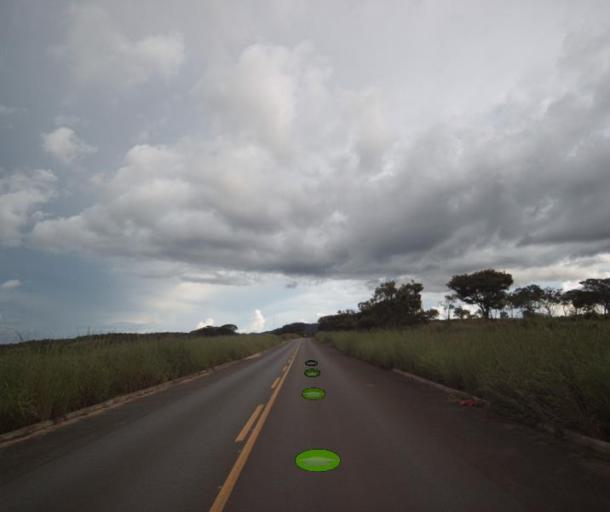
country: BR
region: Goias
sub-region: Niquelandia
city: Niquelandia
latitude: -14.4839
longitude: -48.4888
